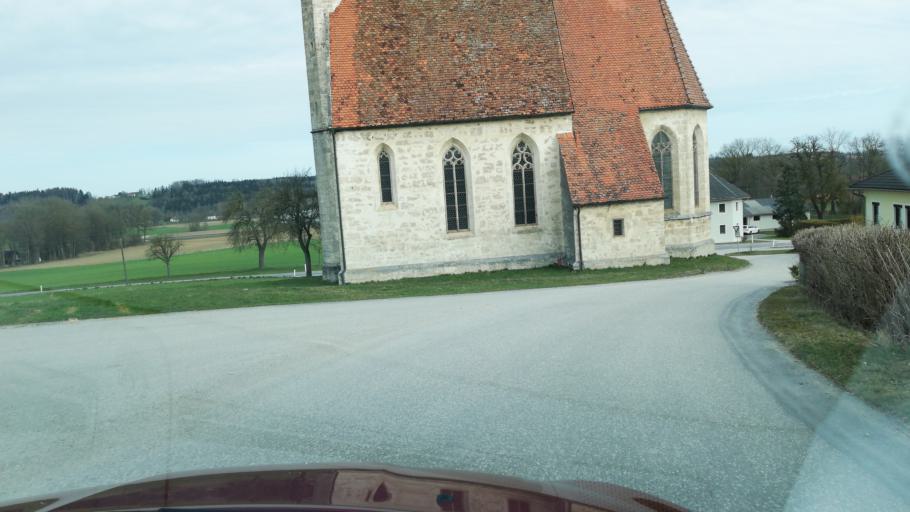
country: AT
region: Upper Austria
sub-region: Politischer Bezirk Steyr-Land
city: Pfarrkirchen bei Bad Hall
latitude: 48.0576
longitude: 14.1707
